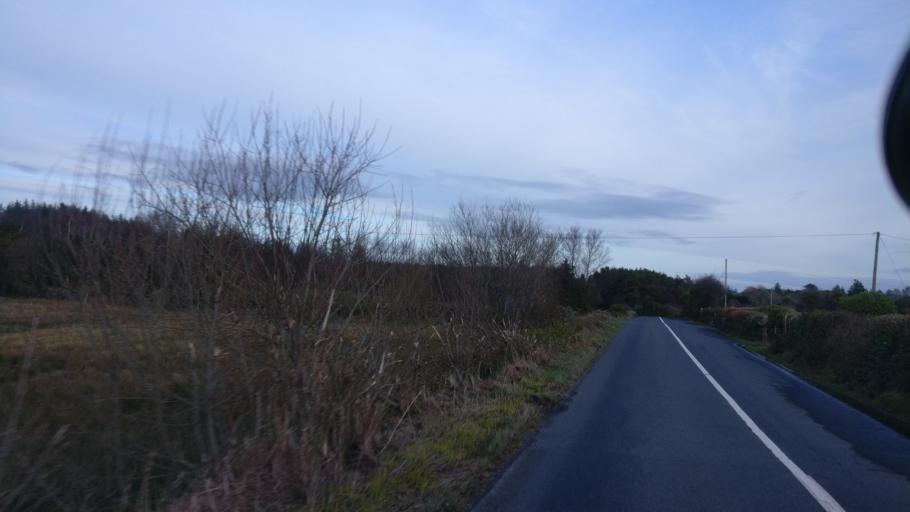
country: IE
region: Connaught
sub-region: County Galway
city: Oughterard
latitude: 53.5313
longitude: -9.3360
